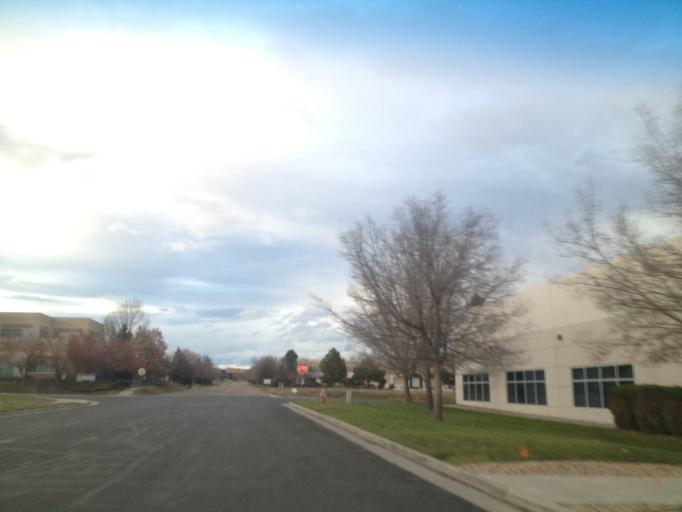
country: US
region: Colorado
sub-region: Boulder County
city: Louisville
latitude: 39.9644
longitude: -105.1196
